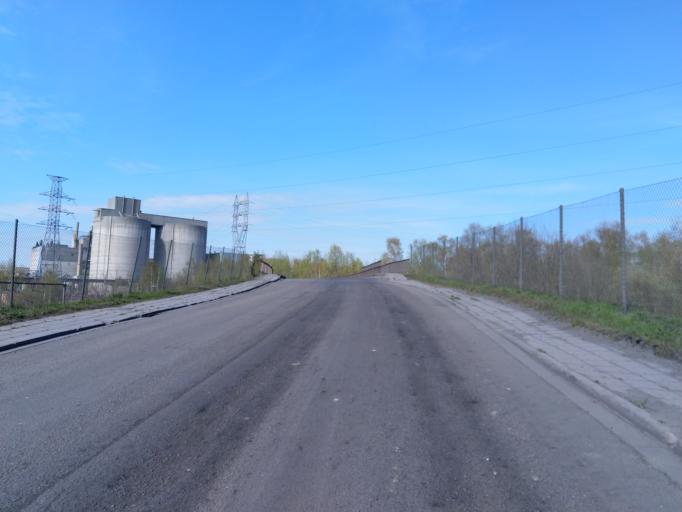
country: BE
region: Wallonia
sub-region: Province du Hainaut
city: Mons
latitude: 50.4691
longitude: 3.9974
